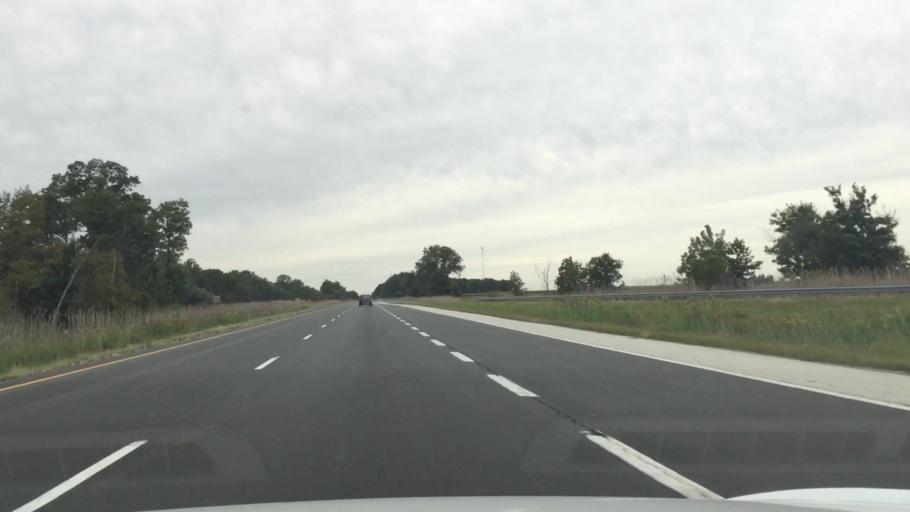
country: CA
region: Ontario
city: Camlachie
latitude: 42.9916
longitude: -82.0059
